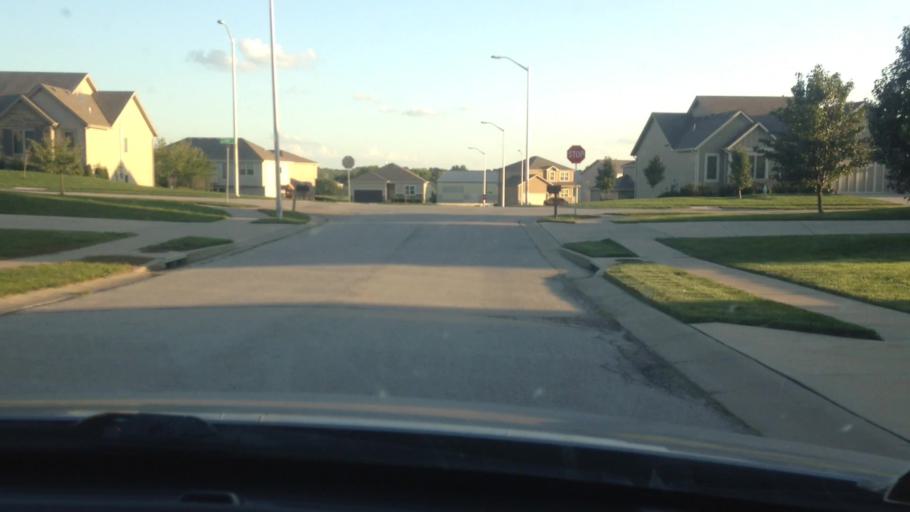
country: US
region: Missouri
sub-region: Clay County
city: Smithville
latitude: 39.2983
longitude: -94.5873
